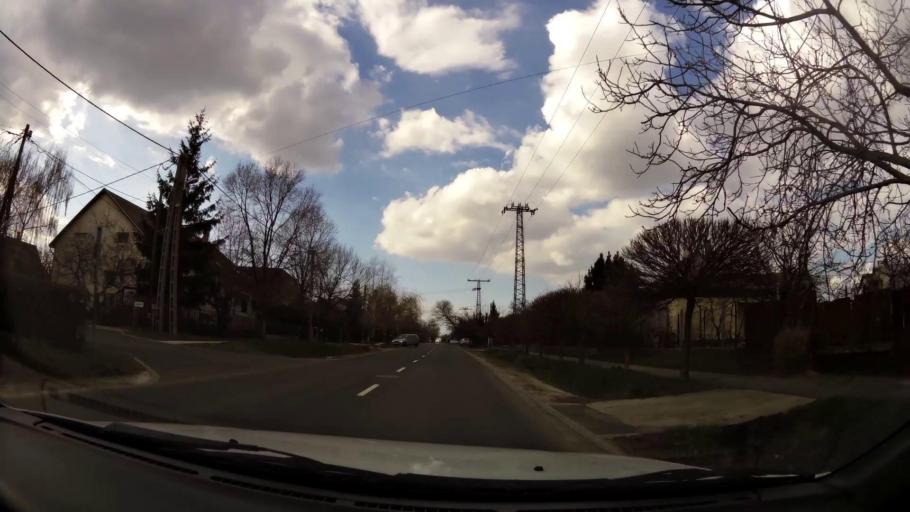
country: HU
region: Budapest
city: Budapest XVII. keruelet
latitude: 47.4975
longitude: 19.2719
